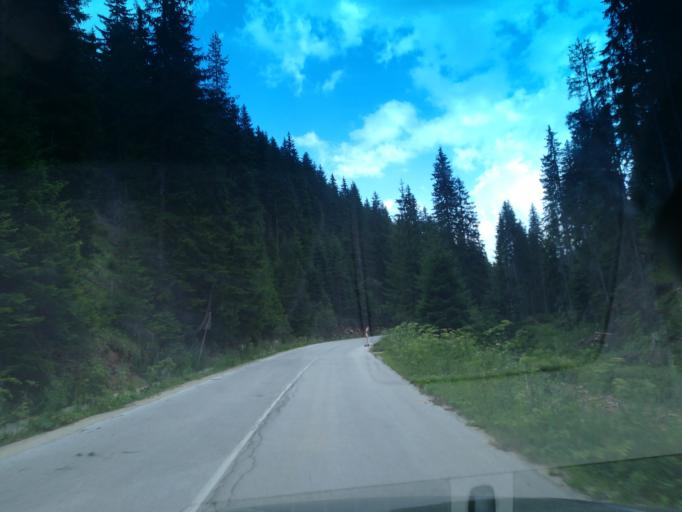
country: BG
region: Smolyan
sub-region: Obshtina Chepelare
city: Chepelare
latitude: 41.6619
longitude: 24.6797
